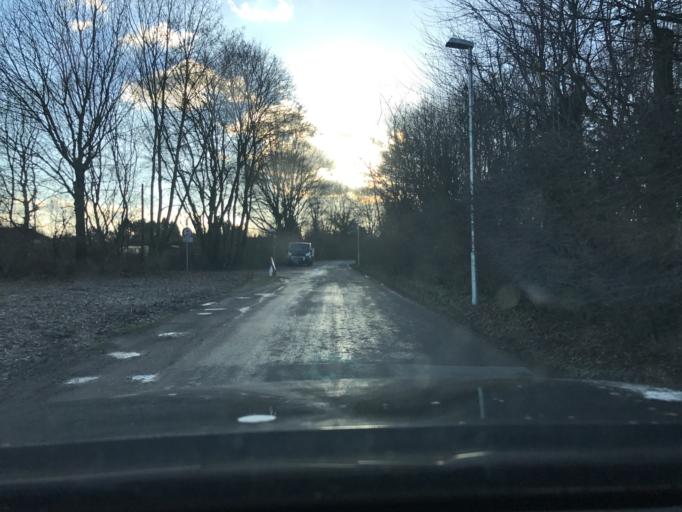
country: DE
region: North Rhine-Westphalia
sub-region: Regierungsbezirk Dusseldorf
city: Krefeld
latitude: 51.3566
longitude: 6.6045
